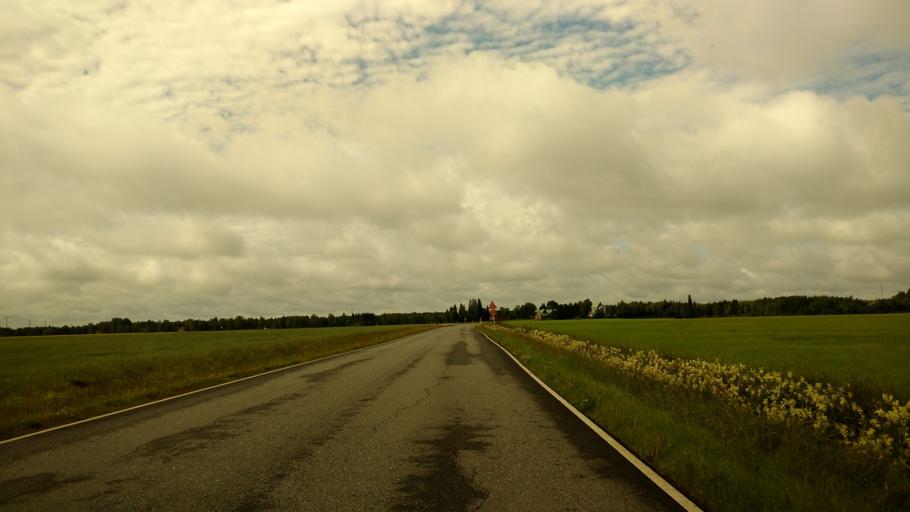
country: FI
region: Varsinais-Suomi
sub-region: Loimaa
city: Koski Tl
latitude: 60.6720
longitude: 23.1576
